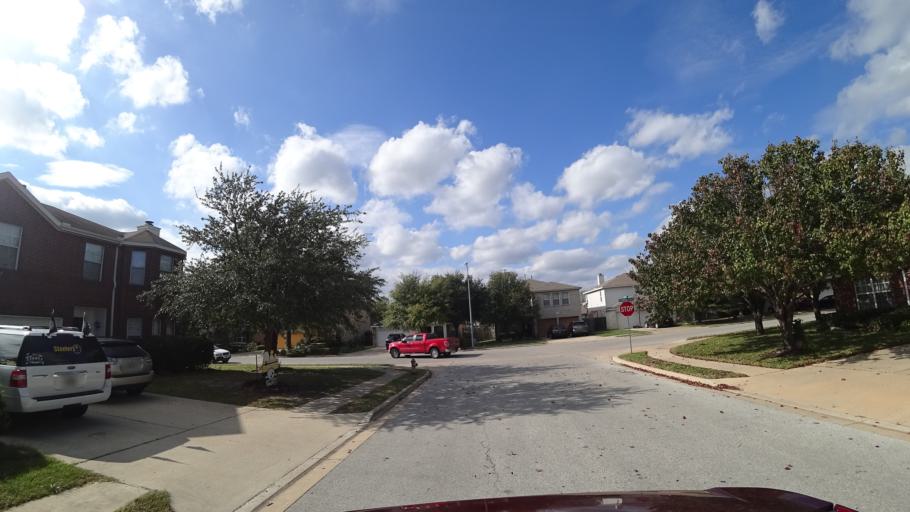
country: US
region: Texas
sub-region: Travis County
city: Pflugerville
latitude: 30.4327
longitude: -97.6375
